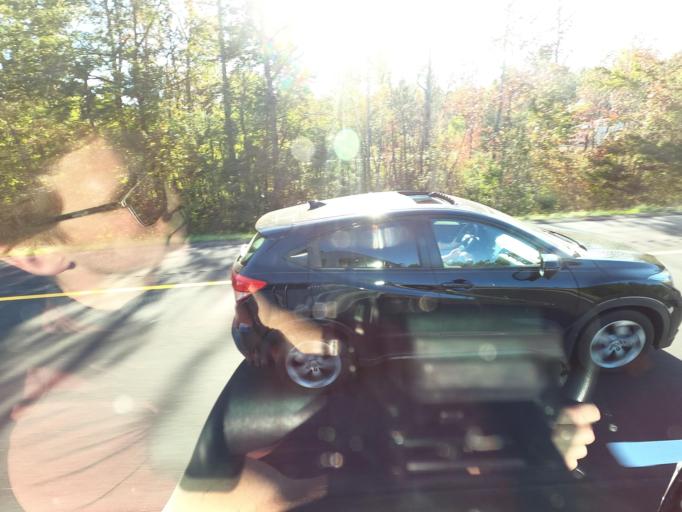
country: US
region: Tennessee
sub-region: Coffee County
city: Manchester
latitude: 35.4276
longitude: -86.0264
